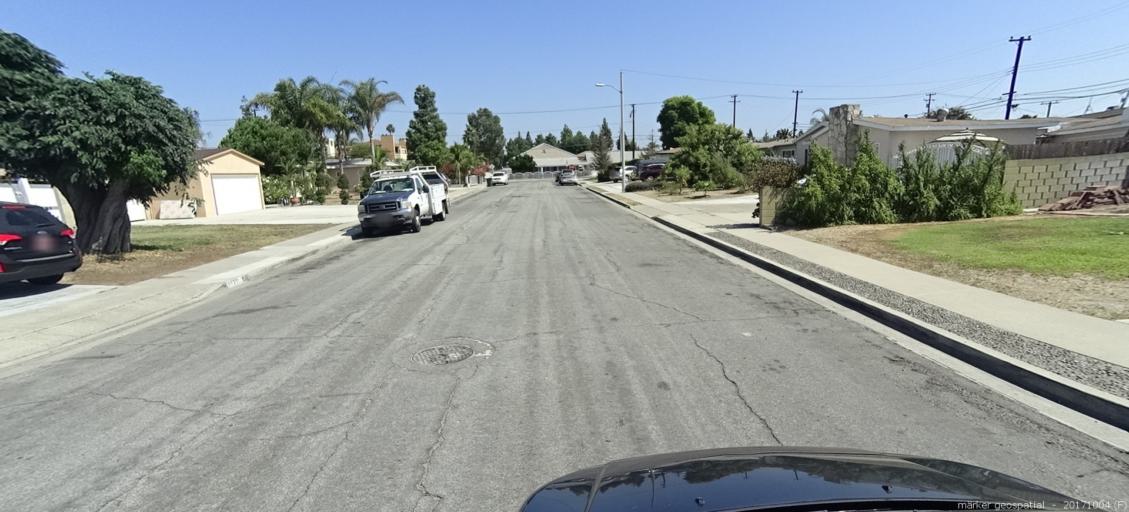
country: US
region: California
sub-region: Orange County
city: Garden Grove
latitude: 33.7799
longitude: -117.9465
